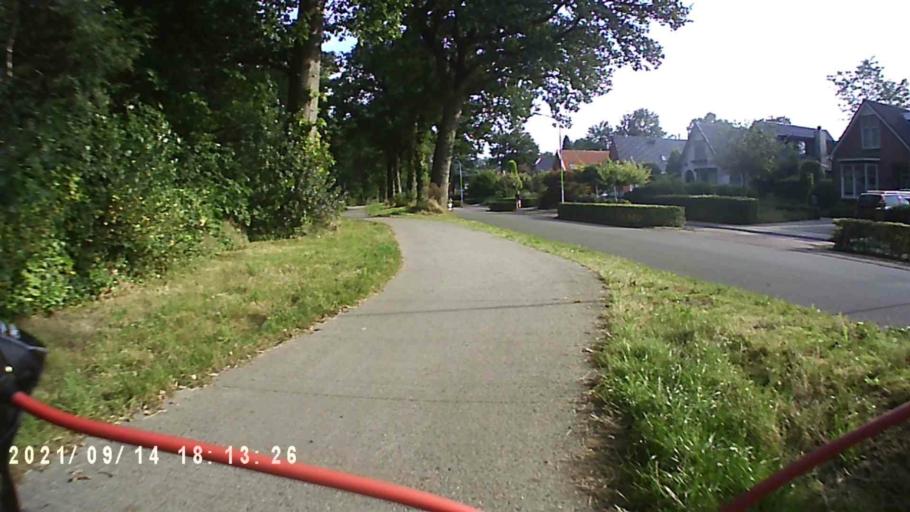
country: NL
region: Drenthe
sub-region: Gemeente Tynaarlo
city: Zuidlaren
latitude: 53.0885
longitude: 6.6660
